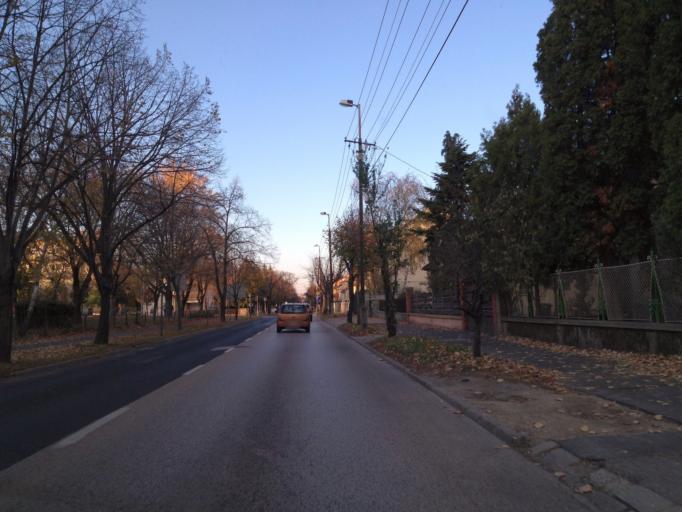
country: HU
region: Gyor-Moson-Sopron
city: Gyor
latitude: 47.6696
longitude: 17.6430
